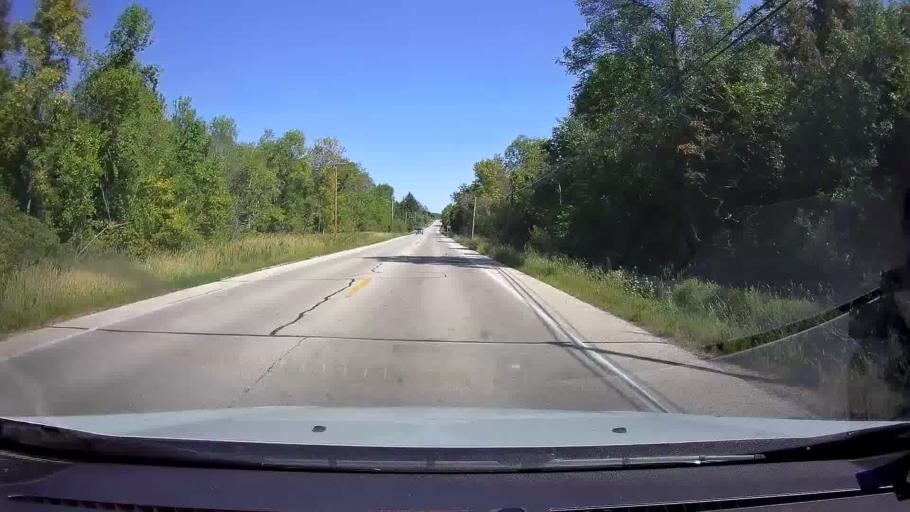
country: US
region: Michigan
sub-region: Delta County
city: Escanaba
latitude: 45.2593
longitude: -87.0549
